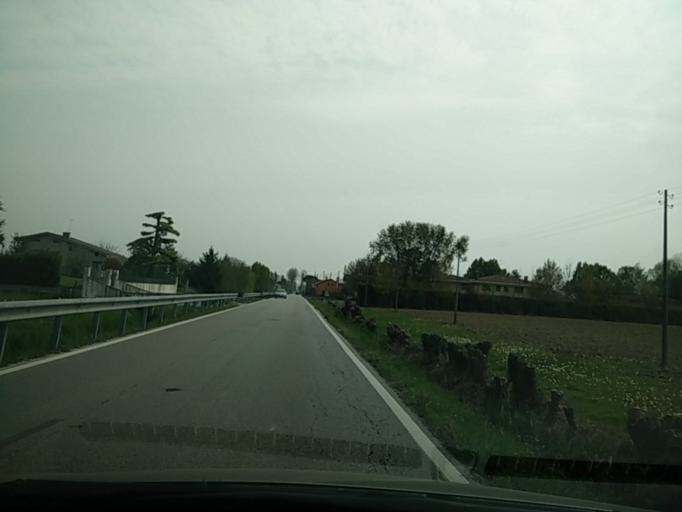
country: IT
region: Veneto
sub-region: Provincia di Venezia
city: Caselle
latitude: 45.4818
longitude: 12.0159
